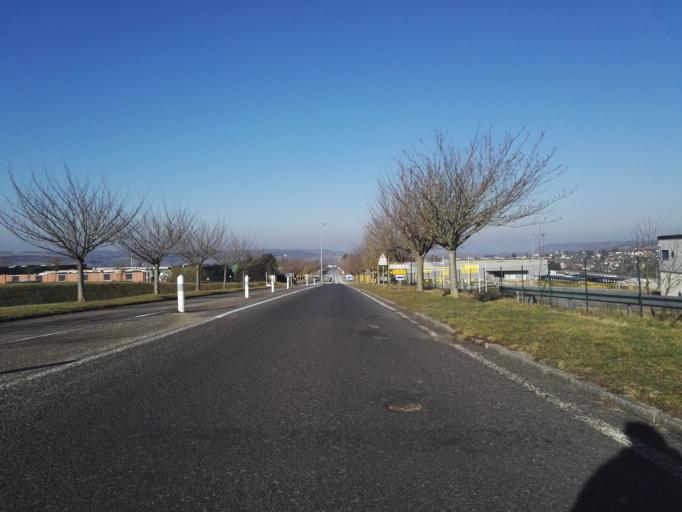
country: FR
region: Haute-Normandie
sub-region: Departement de l'Eure
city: Pacy-sur-Eure
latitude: 49.0089
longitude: 1.4026
